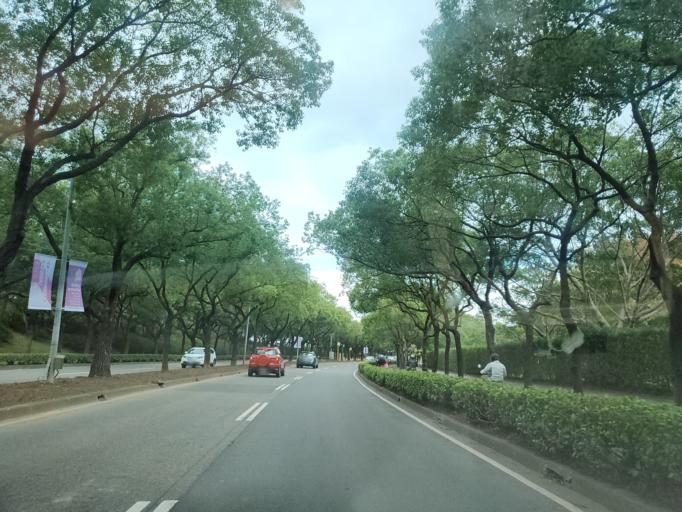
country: TW
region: Taiwan
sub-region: Hsinchu
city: Hsinchu
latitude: 24.7830
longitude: 121.0068
